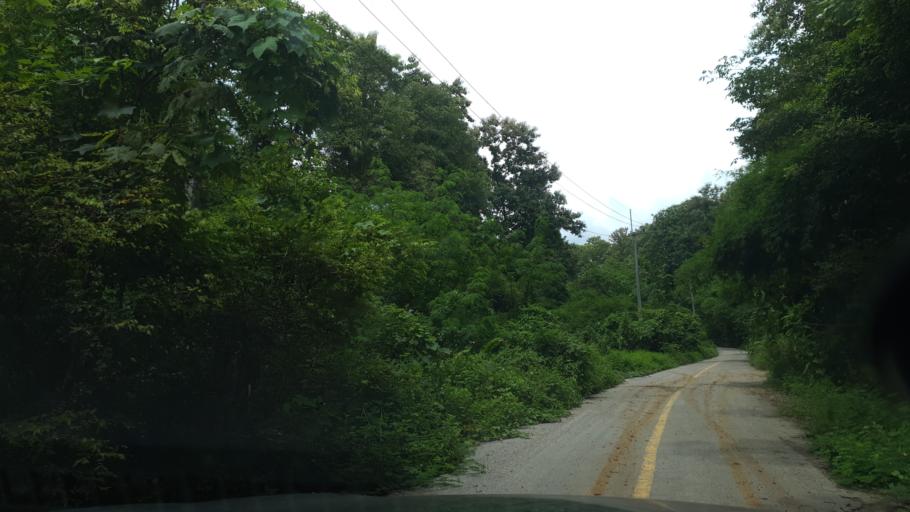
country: TH
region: Lampang
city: Hang Chat
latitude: 18.3504
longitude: 99.2525
